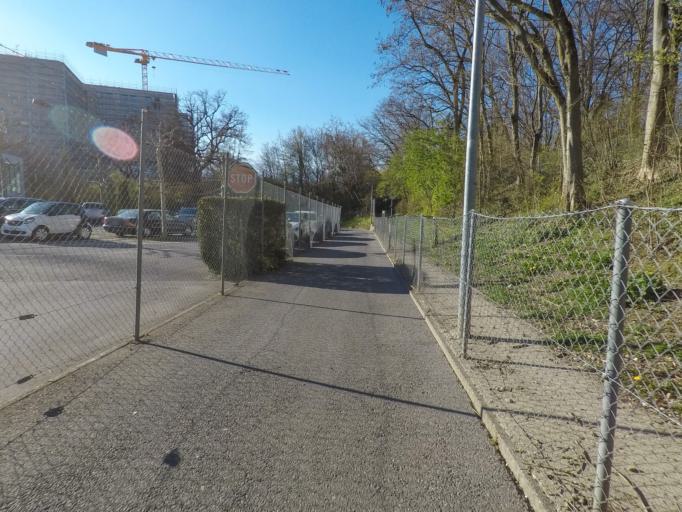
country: CH
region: Geneva
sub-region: Geneva
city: Les Avanchets
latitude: 46.2206
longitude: 6.1054
